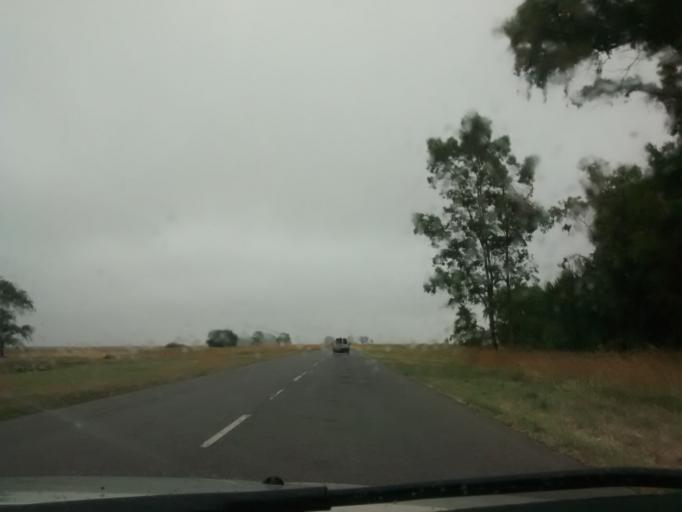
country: AR
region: Buenos Aires
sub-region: Partido de Ayacucho
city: Ayacucho
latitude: -37.4785
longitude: -58.4789
